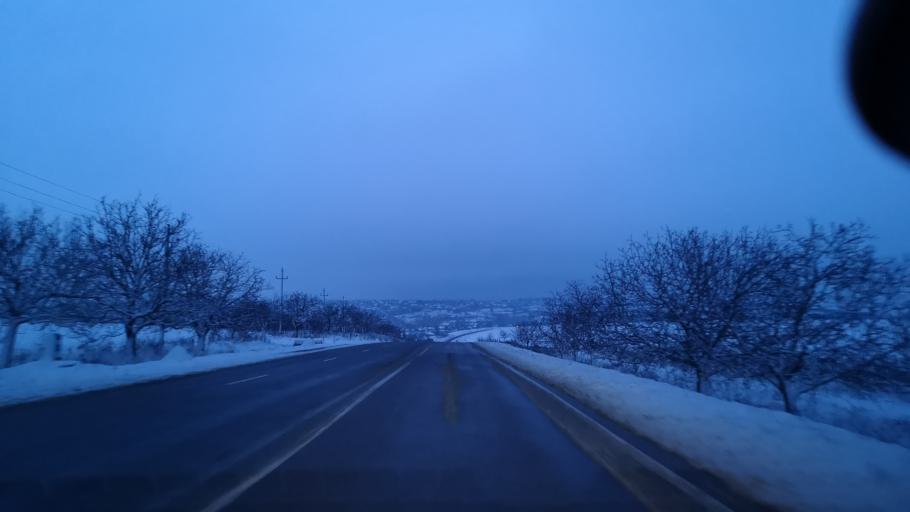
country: MD
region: Soldanesti
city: Soldanesti
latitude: 47.7155
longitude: 28.8474
